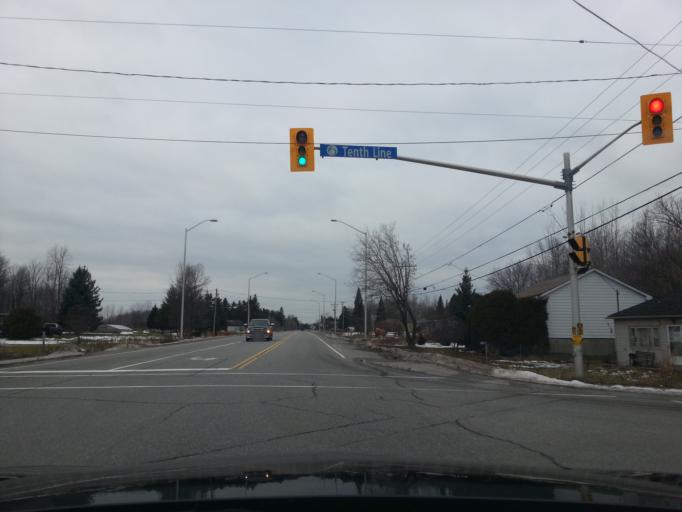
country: CA
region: Ontario
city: Clarence-Rockland
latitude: 45.4218
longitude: -75.4656
